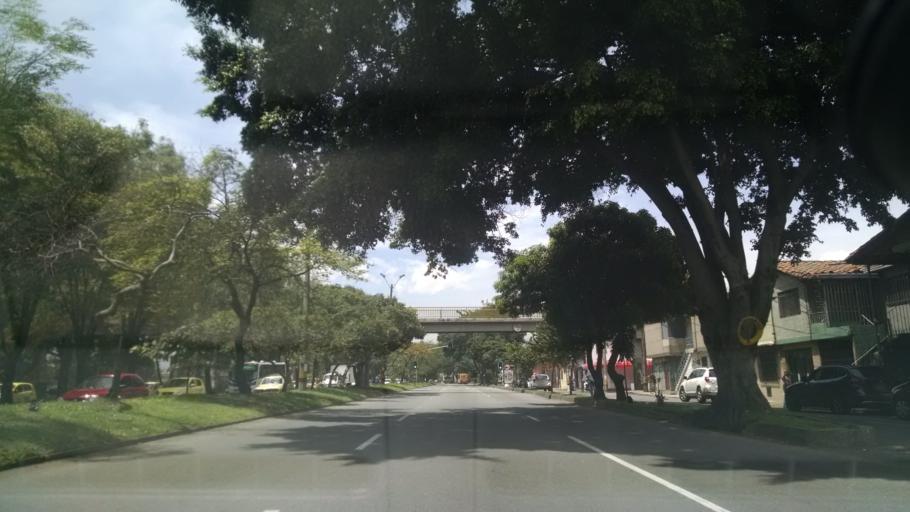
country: CO
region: Antioquia
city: Itagui
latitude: 6.2119
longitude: -75.5837
